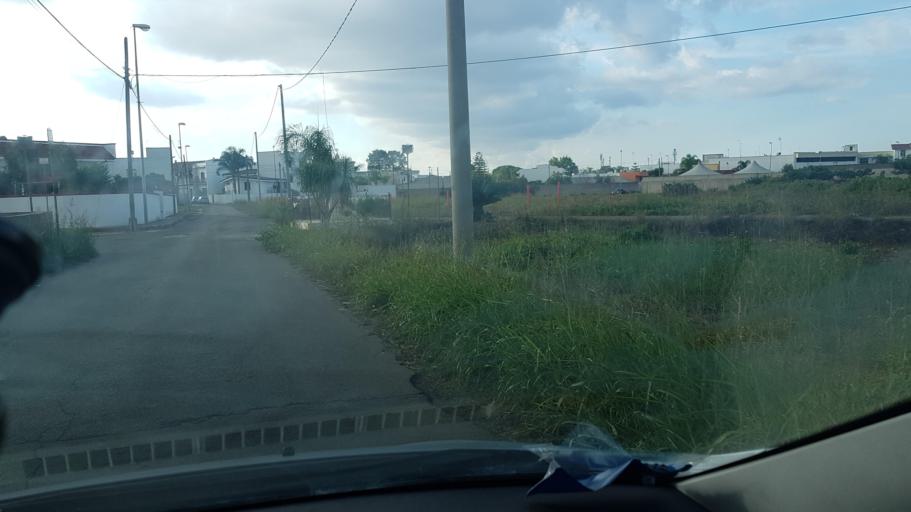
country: IT
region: Apulia
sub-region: Provincia di Brindisi
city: Cellino San Marco
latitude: 40.4706
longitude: 17.9717
